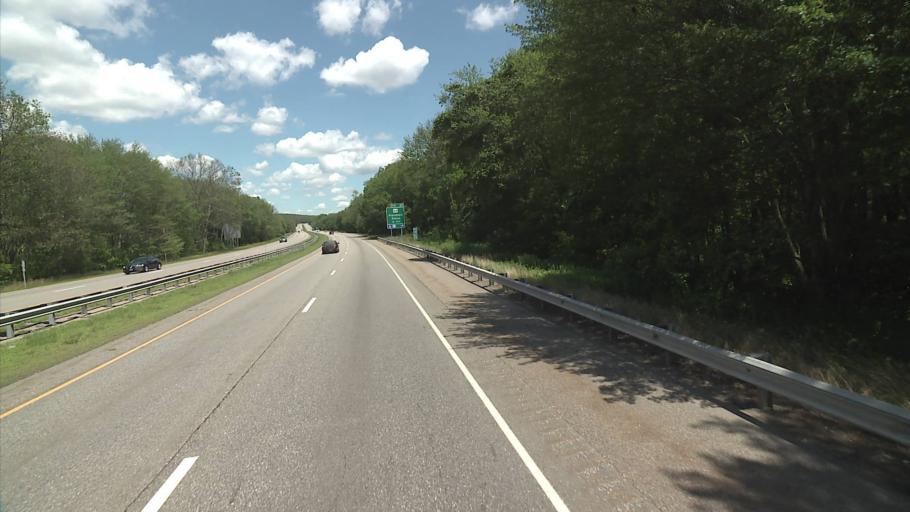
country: US
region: Connecticut
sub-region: Windham County
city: Plainfield
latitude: 41.6724
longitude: -71.9093
